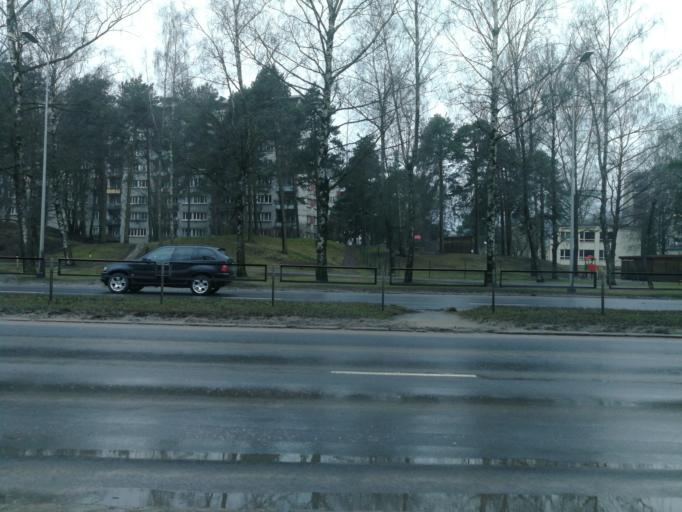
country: LV
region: Riga
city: Jaunciems
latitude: 57.0033
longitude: 24.1300
